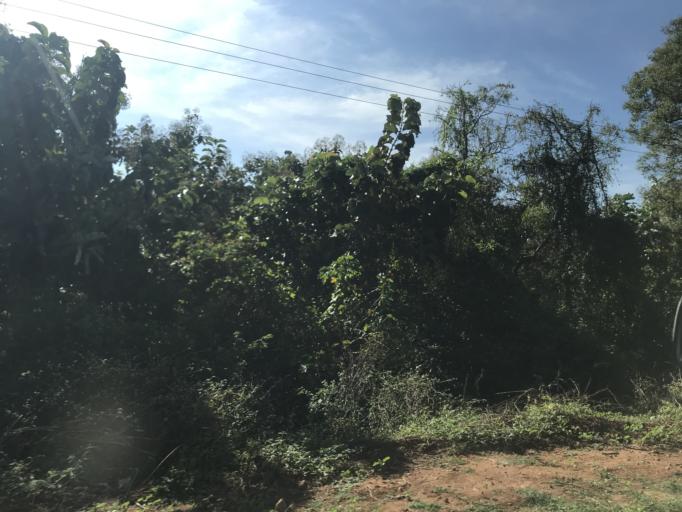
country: IN
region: Karnataka
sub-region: Mysore
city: Mysore
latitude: 12.2157
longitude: 76.5668
